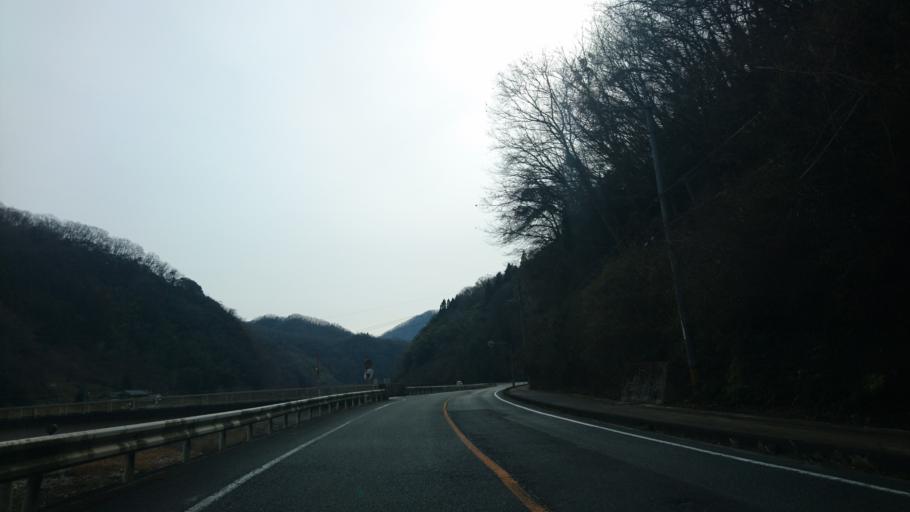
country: JP
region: Okayama
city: Takahashi
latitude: 34.8730
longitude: 133.5624
